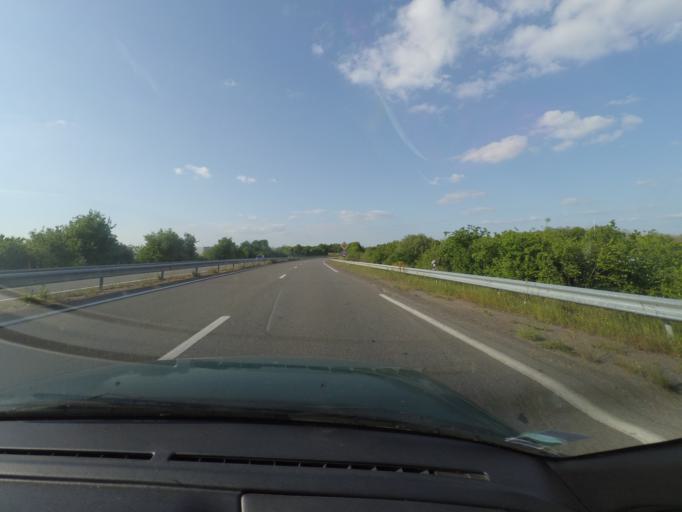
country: FR
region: Pays de la Loire
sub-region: Departement de la Vendee
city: Saligny
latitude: 46.8373
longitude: -1.4199
